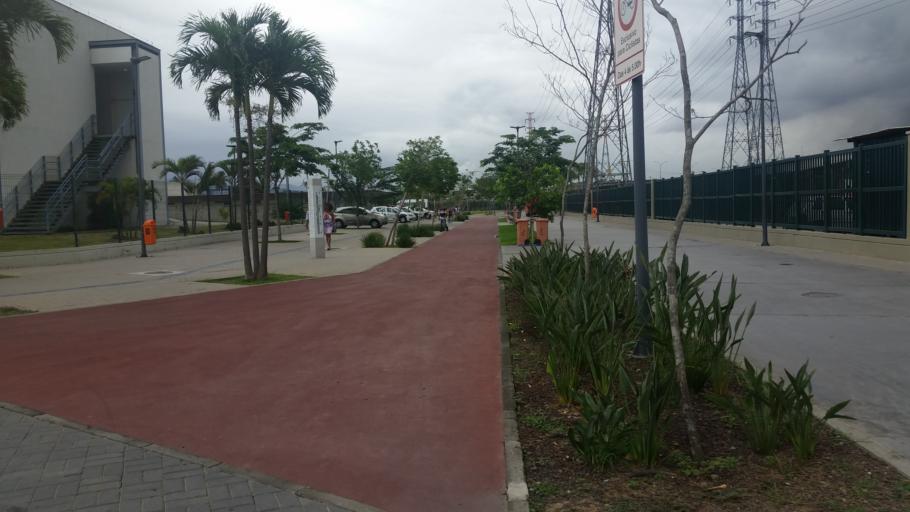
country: BR
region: Rio de Janeiro
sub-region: Sao Joao De Meriti
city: Sao Joao de Meriti
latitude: -22.8617
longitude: -43.3466
